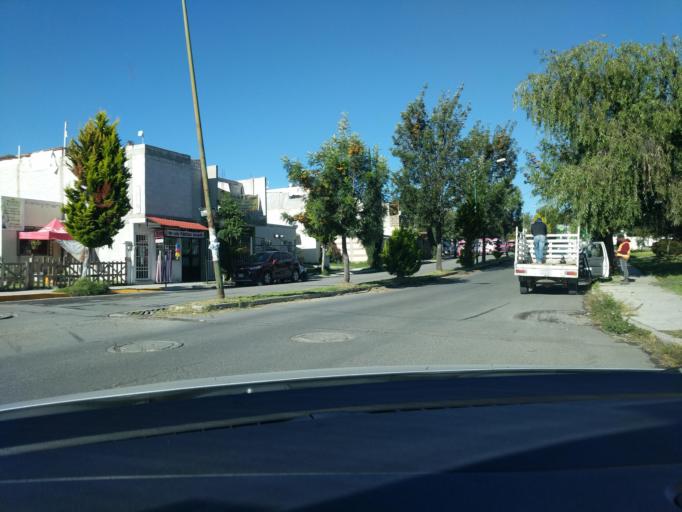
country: MX
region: Puebla
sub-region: Huejotzingo
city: Los Encinos
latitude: 19.1774
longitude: -98.3925
